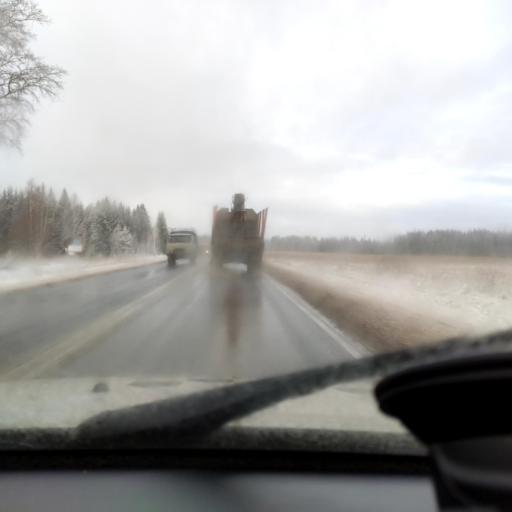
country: RU
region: Perm
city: Nytva
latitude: 57.9609
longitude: 55.3616
